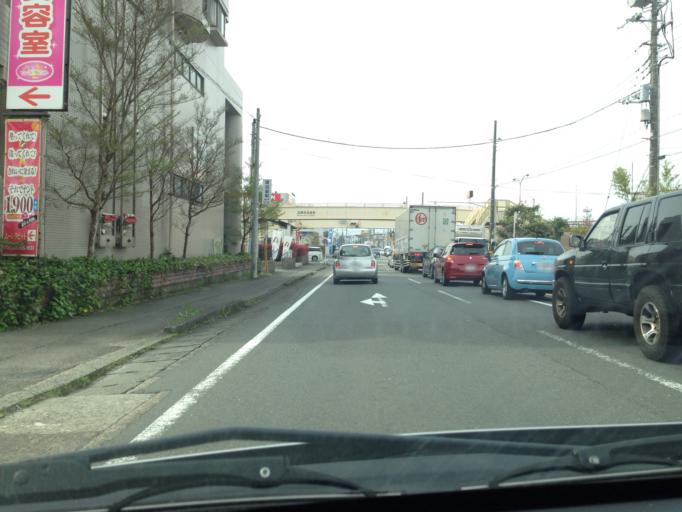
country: JP
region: Shizuoka
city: Numazu
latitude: 35.1219
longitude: 138.8682
